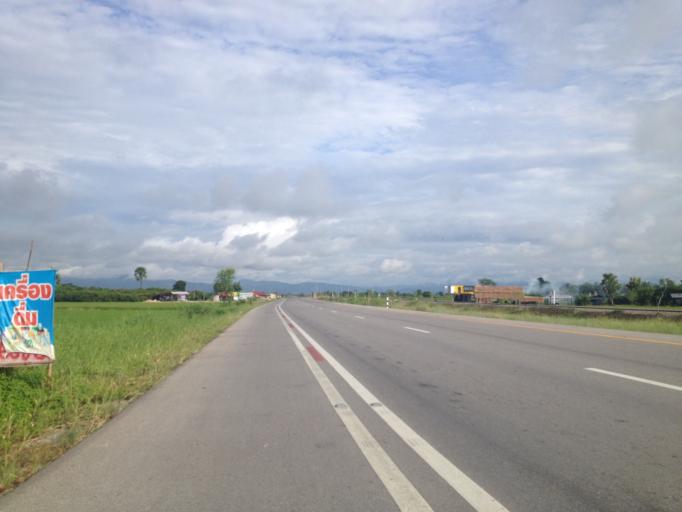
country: TH
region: Chiang Mai
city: San Pa Tong
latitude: 18.5680
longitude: 98.8488
